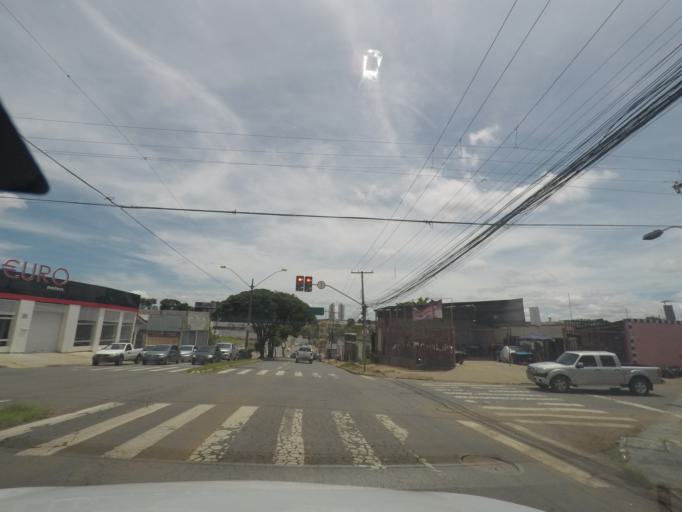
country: BR
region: Goias
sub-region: Goiania
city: Goiania
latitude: -16.6848
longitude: -49.2908
